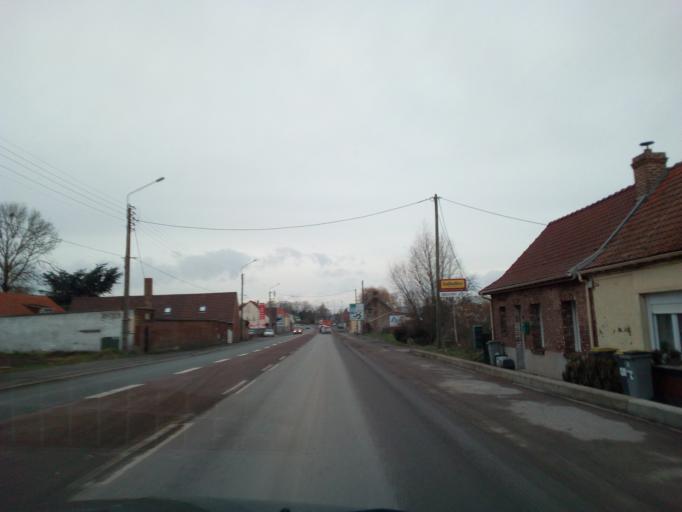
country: FR
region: Nord-Pas-de-Calais
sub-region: Departement du Pas-de-Calais
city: Sailly-Labourse
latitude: 50.5132
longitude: 2.6984
